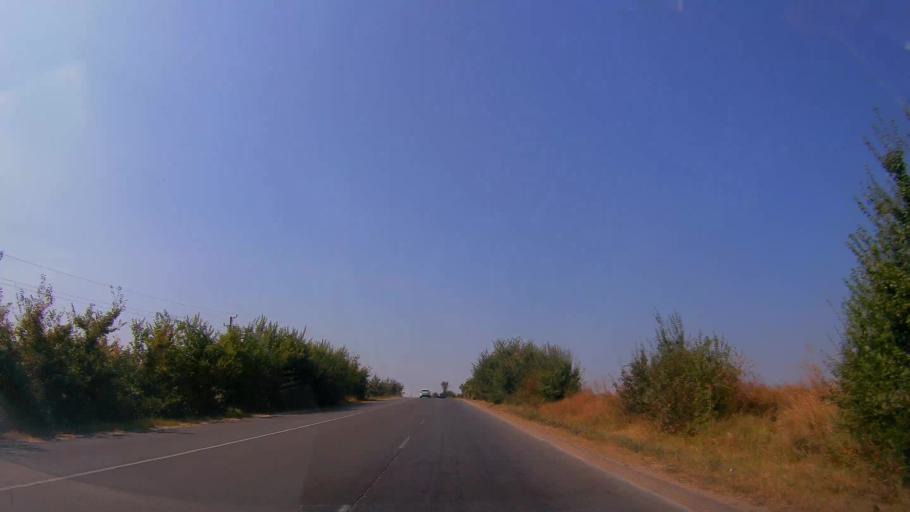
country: BG
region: Ruse
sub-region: Obshtina Vetovo
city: Senovo
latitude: 43.5618
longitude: 26.3627
